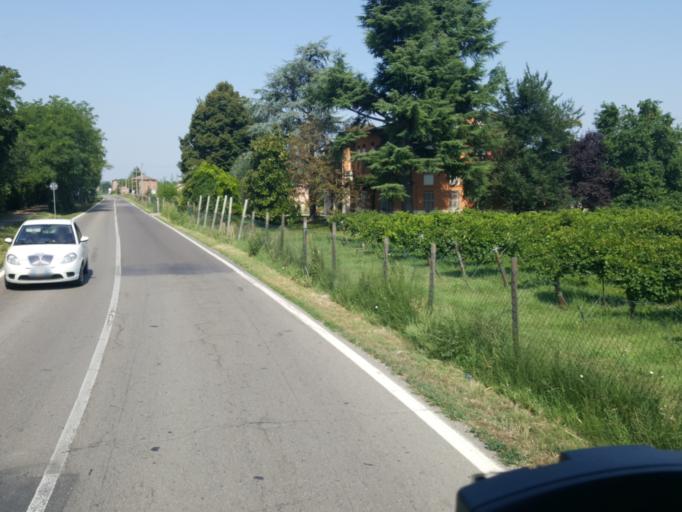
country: IT
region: Emilia-Romagna
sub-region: Provincia di Modena
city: San Vito
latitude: 44.5342
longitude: 10.9831
